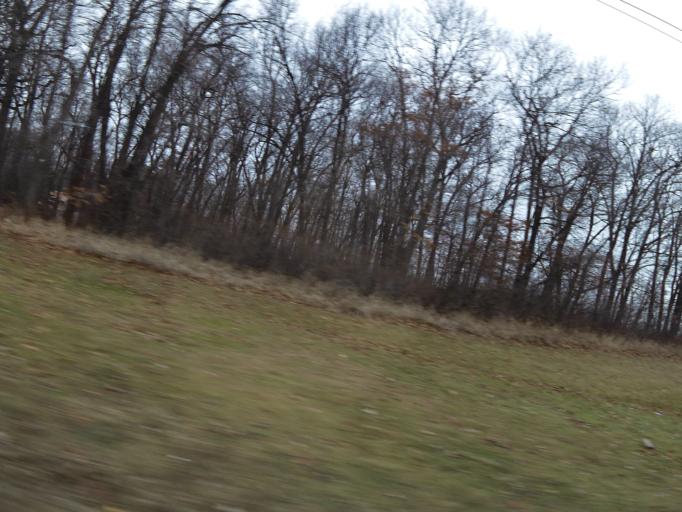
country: US
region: Minnesota
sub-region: Scott County
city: Prior Lake
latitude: 44.7467
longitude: -93.4005
